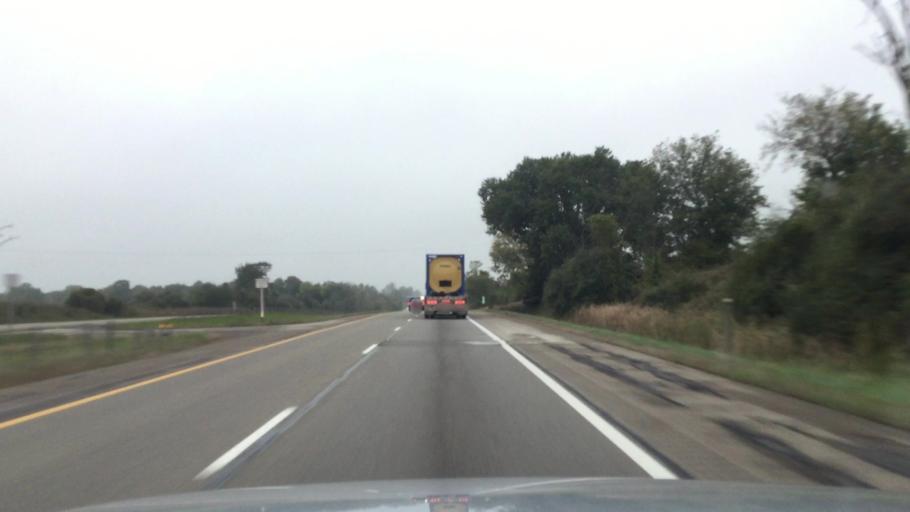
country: US
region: Michigan
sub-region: Shiawassee County
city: Durand
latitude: 42.9087
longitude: -84.0547
